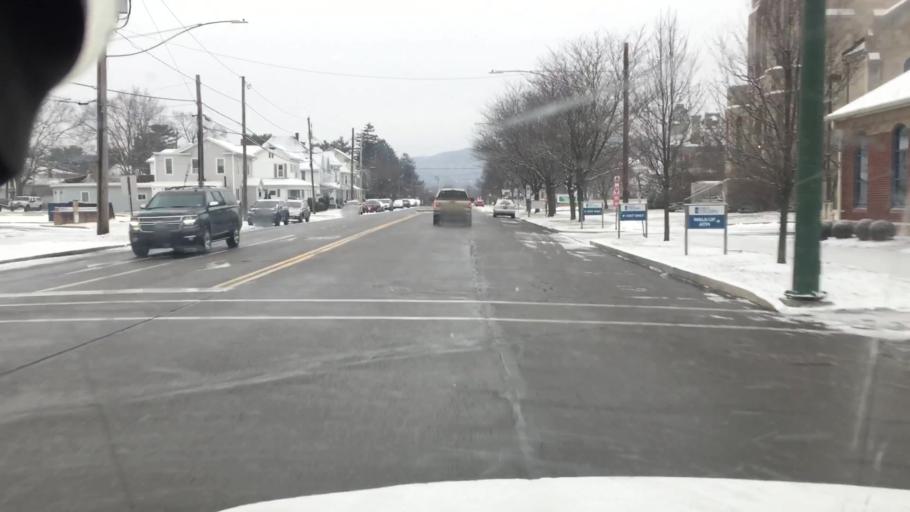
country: US
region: Pennsylvania
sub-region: Columbia County
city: Berwick
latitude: 41.0559
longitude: -76.2345
